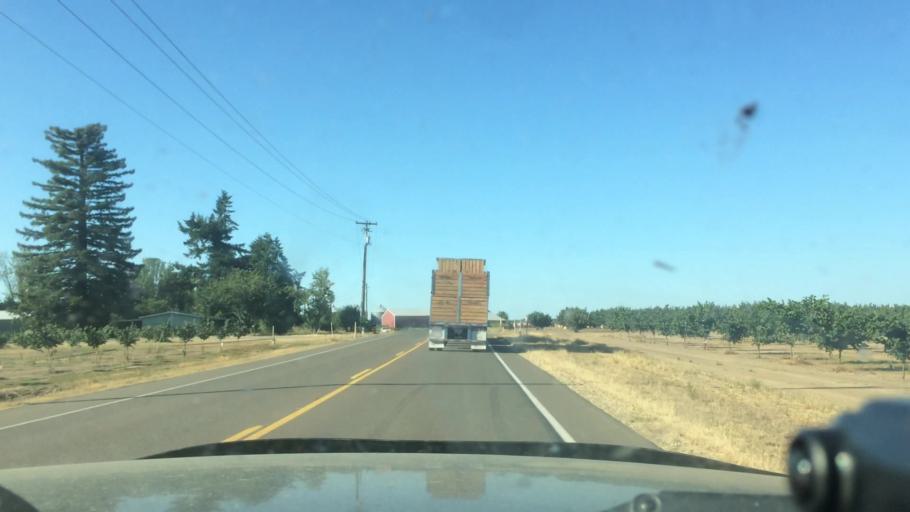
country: US
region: Oregon
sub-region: Marion County
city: Gervais
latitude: 45.0773
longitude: -122.9767
